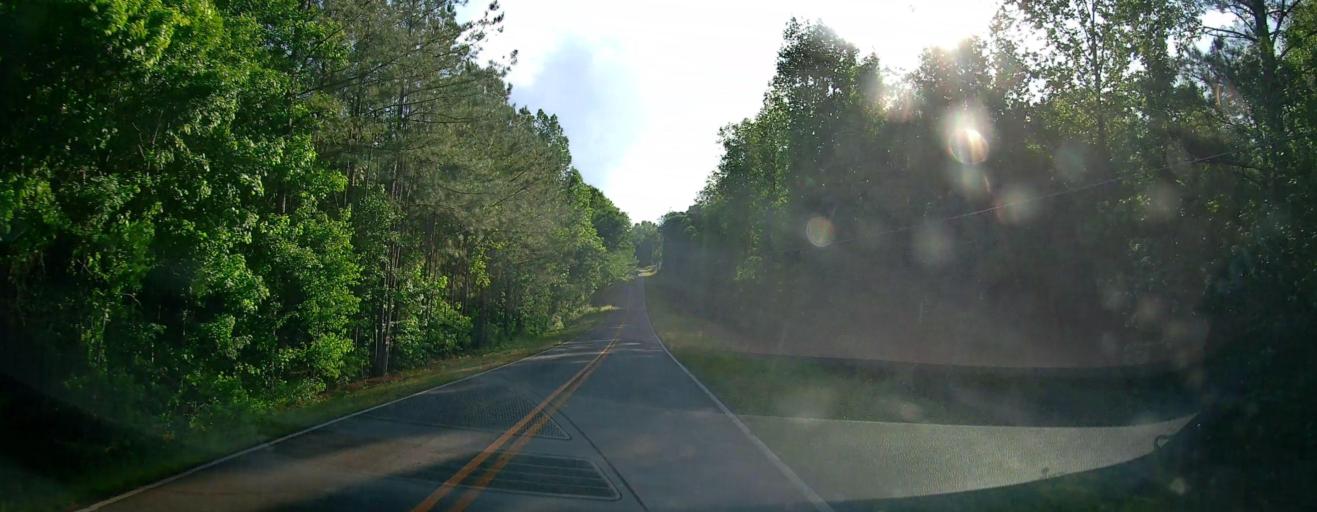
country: US
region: Georgia
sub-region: Peach County
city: Byron
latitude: 32.6776
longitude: -83.7785
